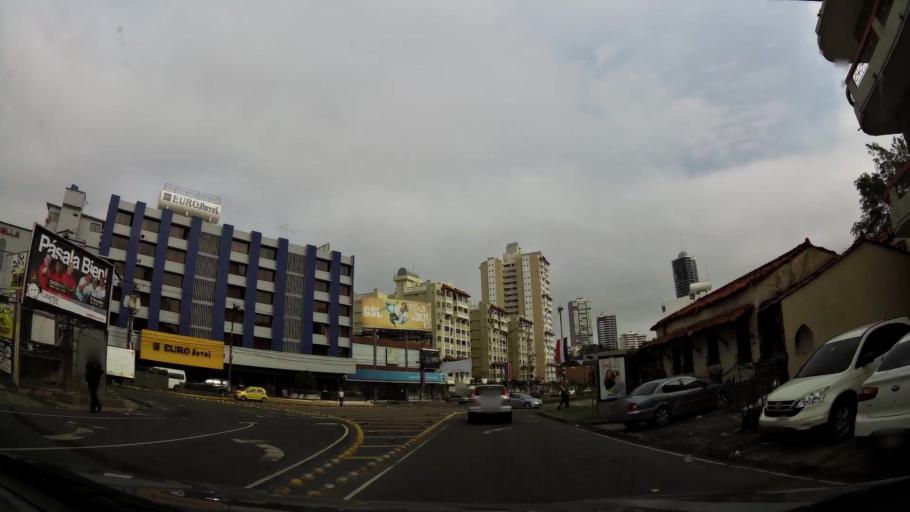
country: PA
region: Panama
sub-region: Distrito de Panama
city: Ancon
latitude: 8.9748
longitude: -79.5345
